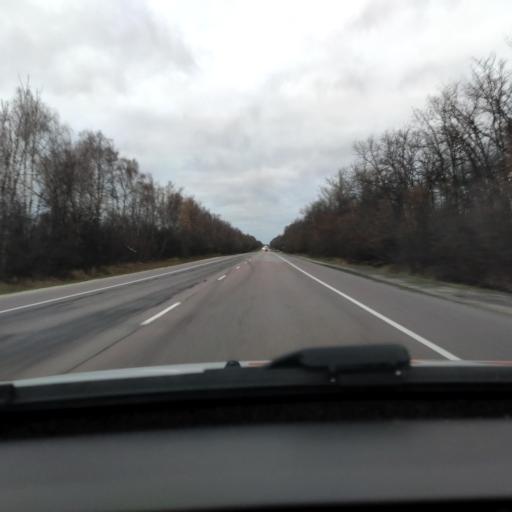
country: RU
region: Lipetsk
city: Khlevnoye
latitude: 52.2924
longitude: 39.1674
